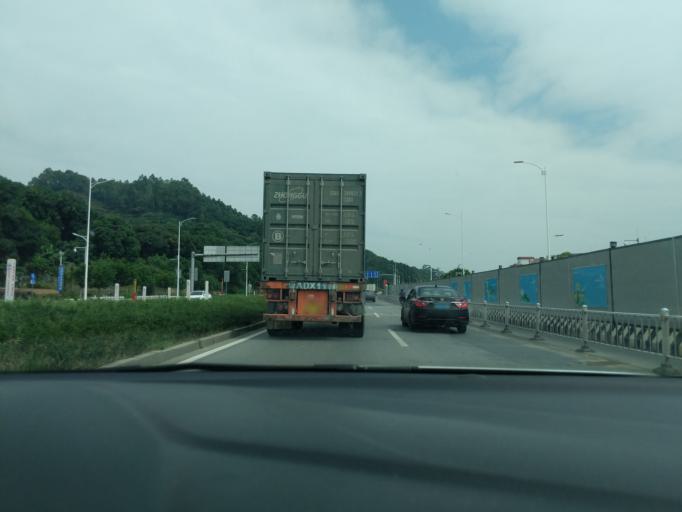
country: CN
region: Guangdong
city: Nansha
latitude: 22.7555
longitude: 113.5694
